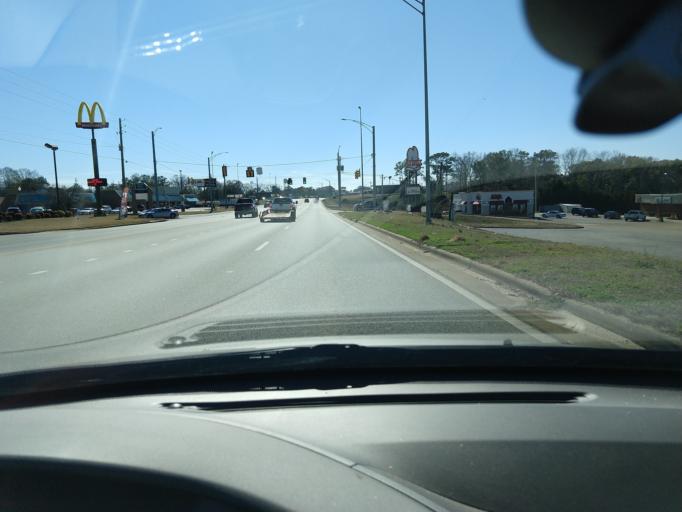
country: US
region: Alabama
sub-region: Covington County
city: Andalusia
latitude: 31.3087
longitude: -86.4995
